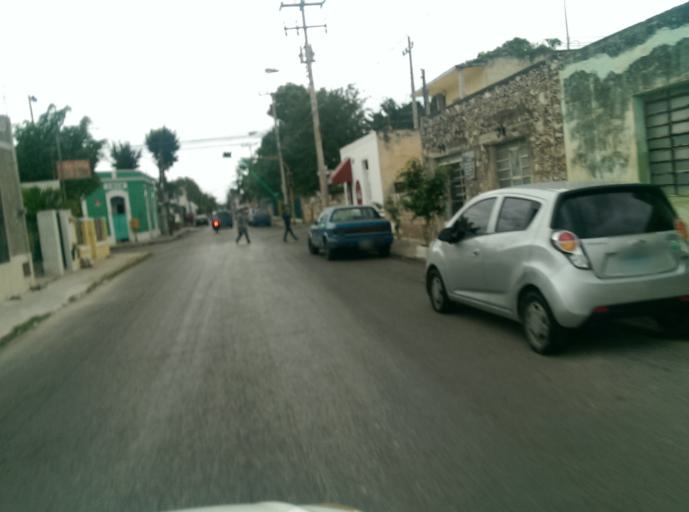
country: MX
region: Yucatan
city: Merida
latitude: 20.9781
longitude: -89.6360
